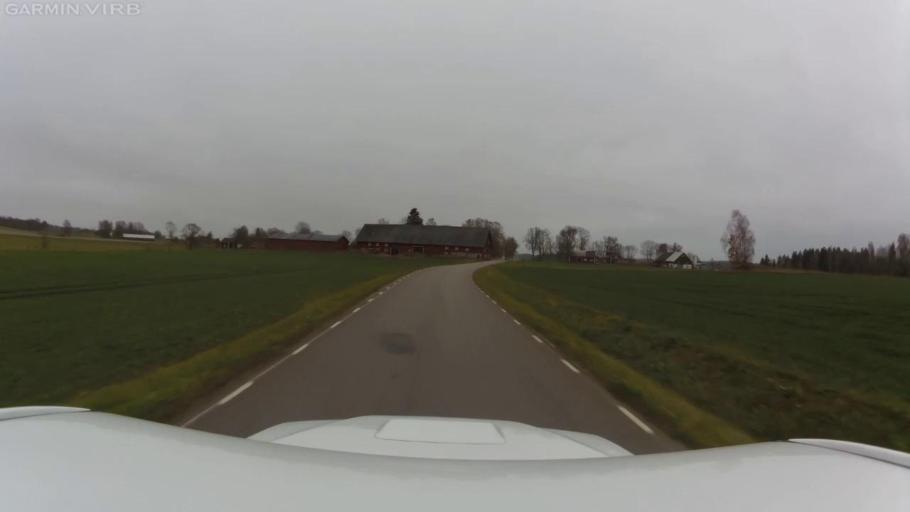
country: SE
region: OEstergoetland
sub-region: Linkopings Kommun
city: Vikingstad
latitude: 58.3102
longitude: 15.3800
